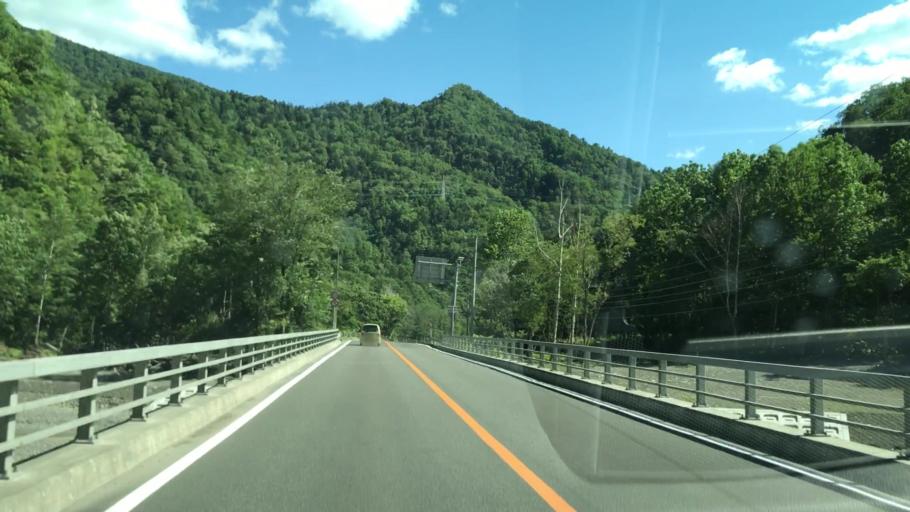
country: JP
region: Hokkaido
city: Shimo-furano
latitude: 42.9166
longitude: 142.5866
